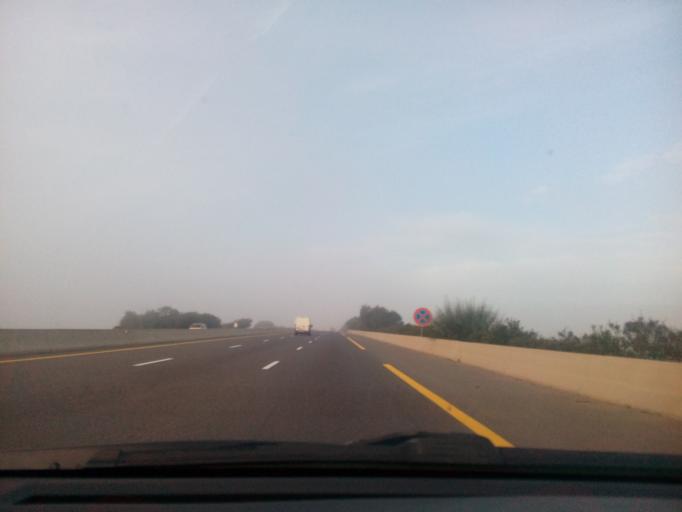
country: DZ
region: Relizane
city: Relizane
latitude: 35.7910
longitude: 0.4610
